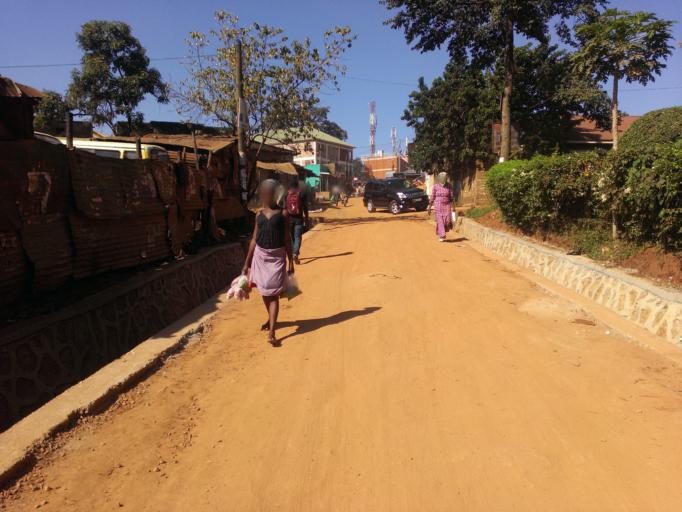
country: UG
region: Central Region
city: Kampala Central Division
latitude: 0.3270
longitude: 32.5618
